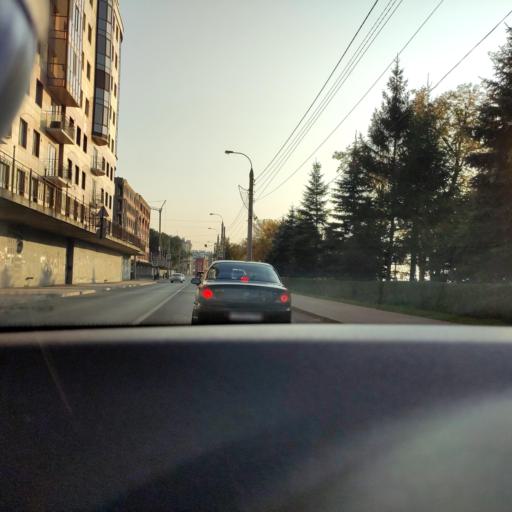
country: RU
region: Samara
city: Rozhdestveno
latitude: 53.1945
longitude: 50.0888
